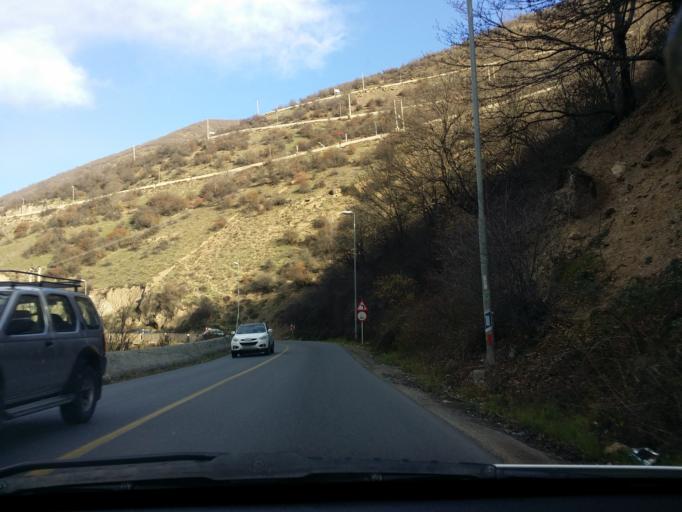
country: IR
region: Mazandaran
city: Chalus
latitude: 36.2670
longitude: 51.2588
